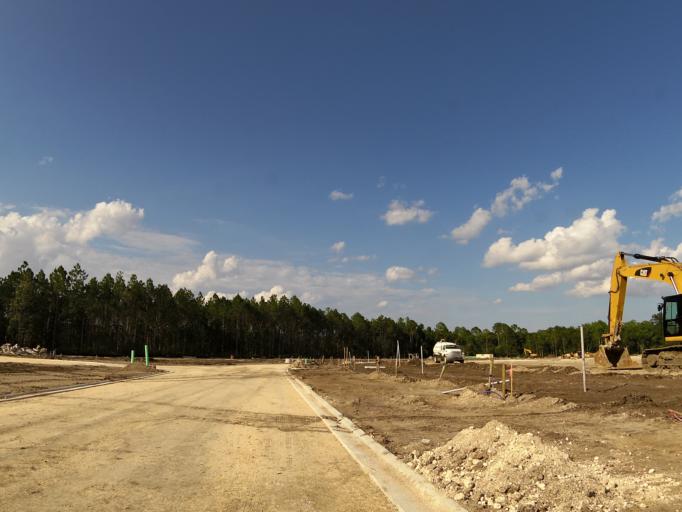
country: US
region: Florida
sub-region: Clay County
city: Green Cove Springs
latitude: 30.0338
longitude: -81.6318
